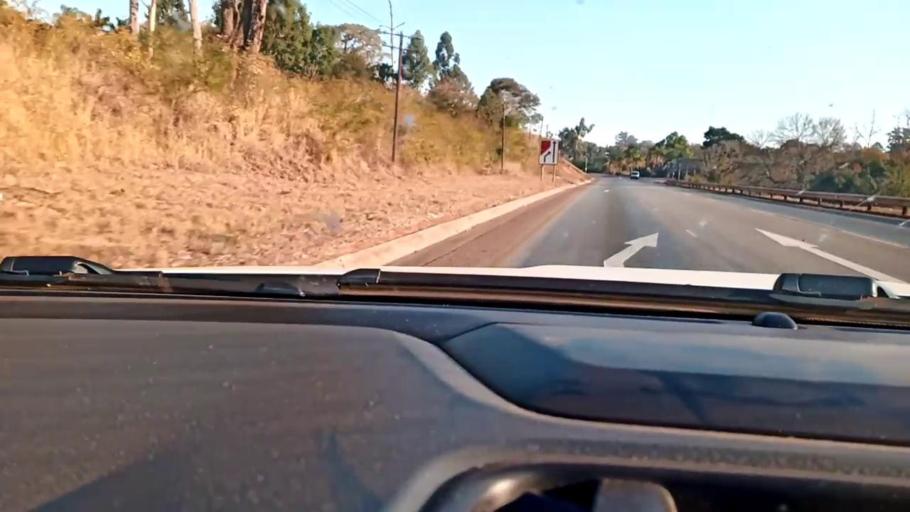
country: ZA
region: Limpopo
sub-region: Mopani District Municipality
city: Duiwelskloof
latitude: -23.6880
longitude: 30.1475
